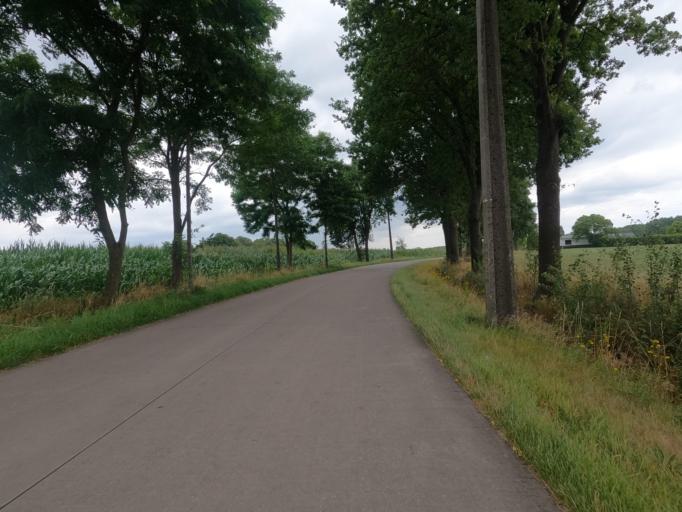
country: BE
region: Flanders
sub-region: Provincie Antwerpen
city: Rijkevorsel
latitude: 51.3702
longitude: 4.7619
